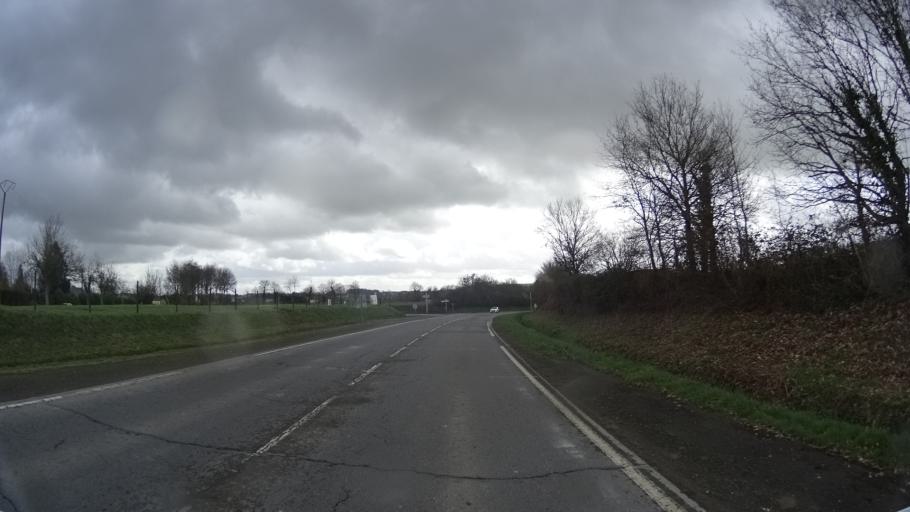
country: FR
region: Brittany
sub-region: Departement d'Ille-et-Vilaine
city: Saint-Gilles
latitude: 48.1622
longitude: -1.8361
